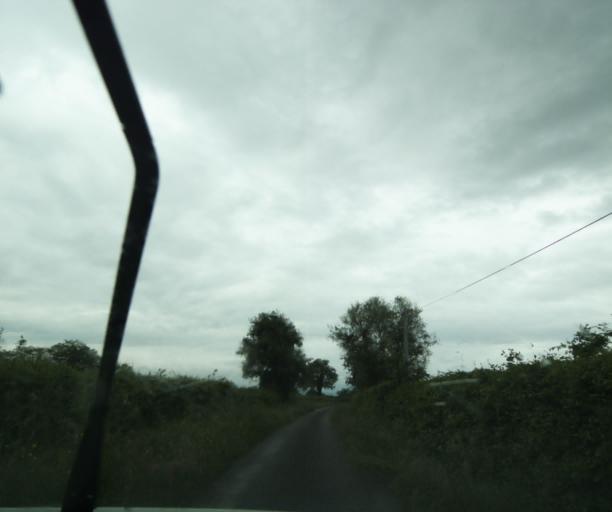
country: FR
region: Bourgogne
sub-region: Departement de Saone-et-Loire
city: Ciry-le-Noble
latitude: 46.5344
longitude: 4.2984
